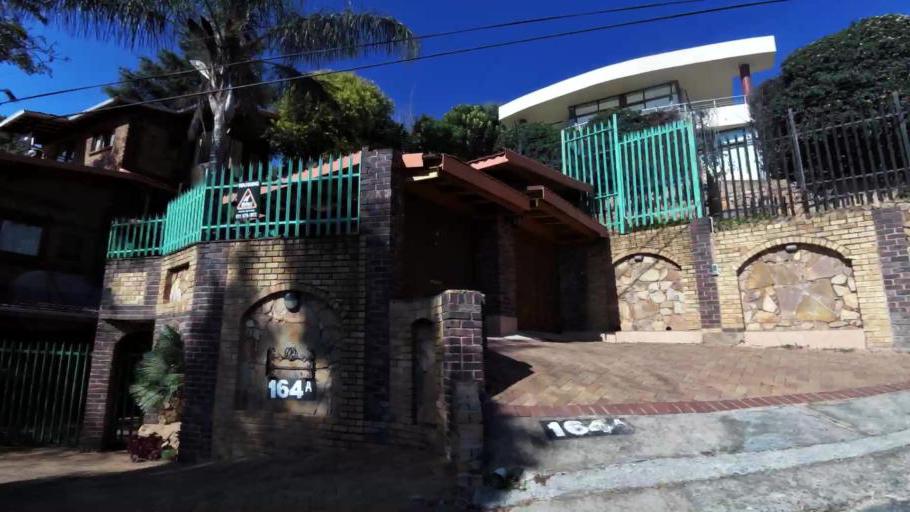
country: ZA
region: Gauteng
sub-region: City of Johannesburg Metropolitan Municipality
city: Roodepoort
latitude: -26.1454
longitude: 27.9631
